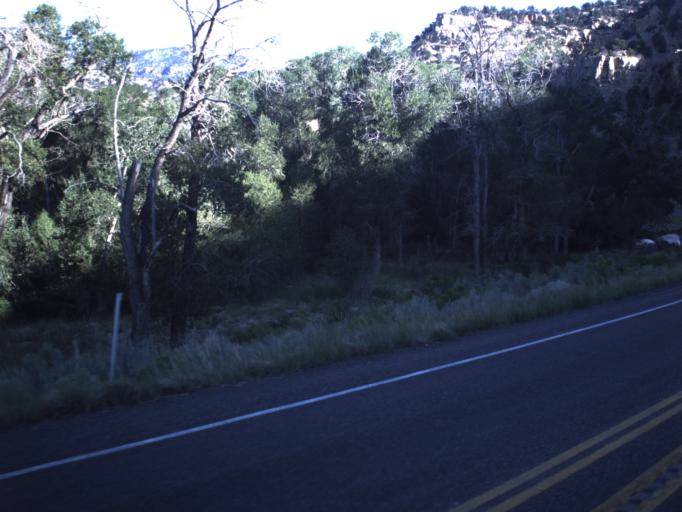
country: US
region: Utah
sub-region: Emery County
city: Huntington
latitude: 39.4010
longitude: -111.1093
